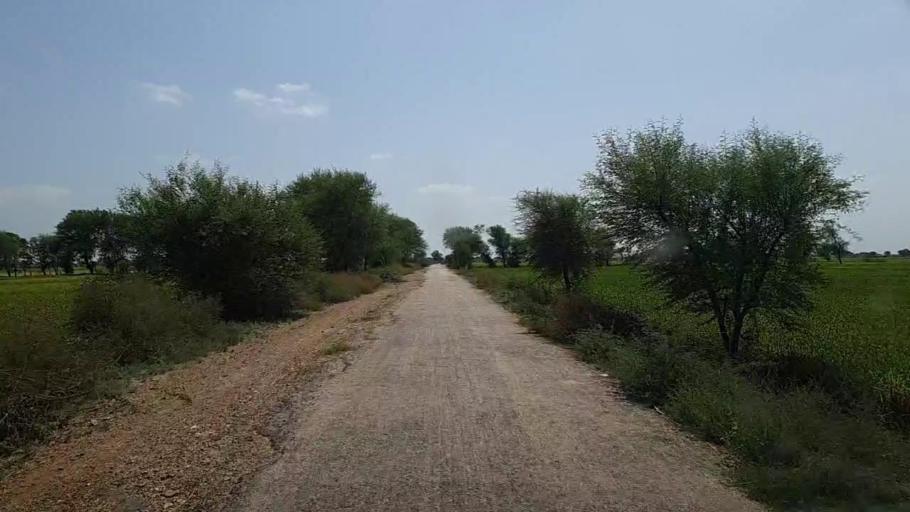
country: PK
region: Sindh
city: Kario
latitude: 24.6473
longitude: 68.5640
